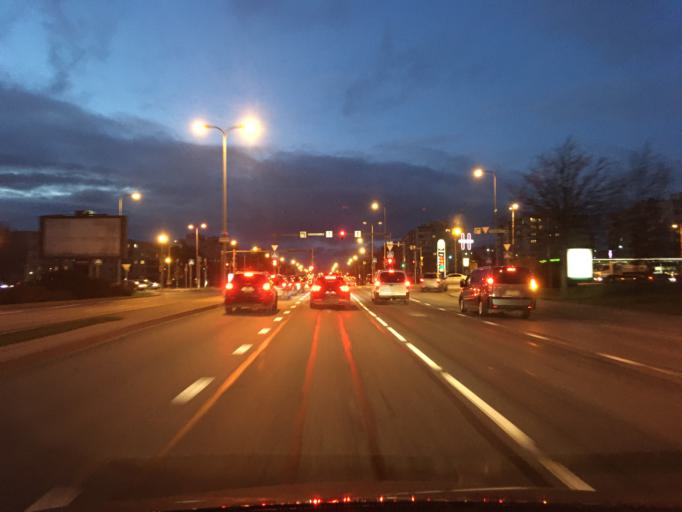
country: EE
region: Harju
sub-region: Tallinna linn
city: Kose
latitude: 59.4334
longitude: 24.8317
